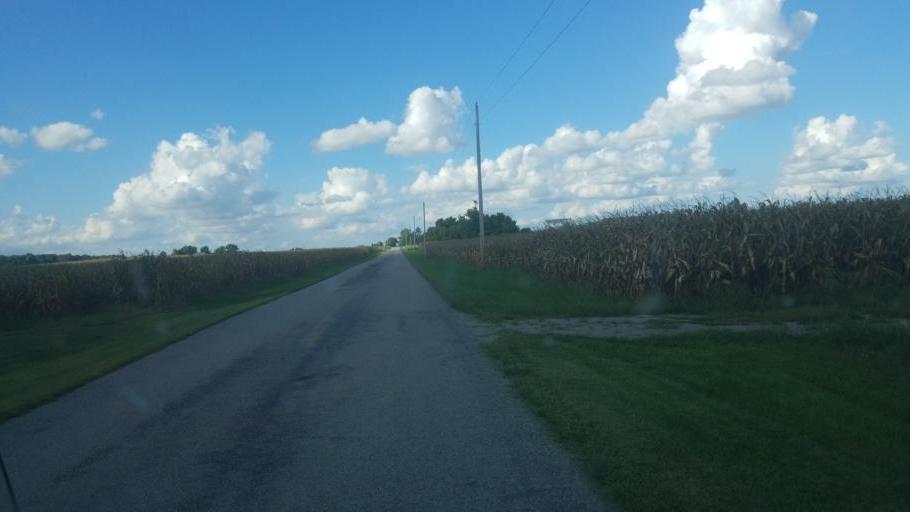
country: US
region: Ohio
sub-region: Hardin County
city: Kenton
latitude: 40.7106
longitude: -83.6918
